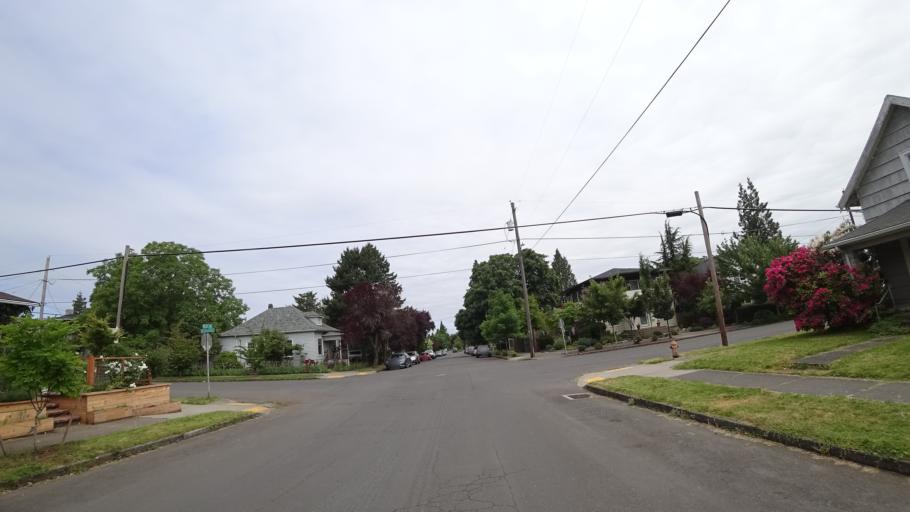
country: US
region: Oregon
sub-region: Multnomah County
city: Portland
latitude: 45.5612
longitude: -122.6338
